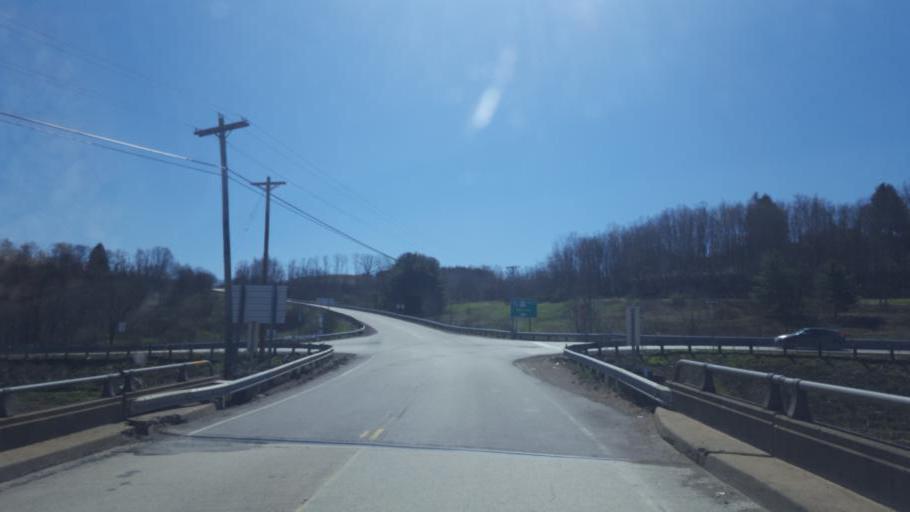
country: US
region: Ohio
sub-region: Belmont County
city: Barnesville
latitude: 40.0524
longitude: -81.3245
